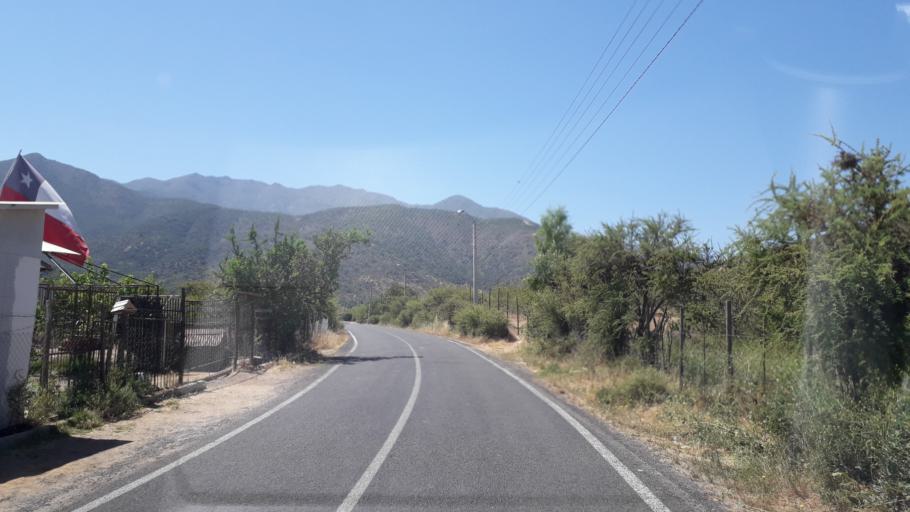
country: CL
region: Valparaiso
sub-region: Provincia de Marga Marga
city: Limache
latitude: -33.0669
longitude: -71.2219
